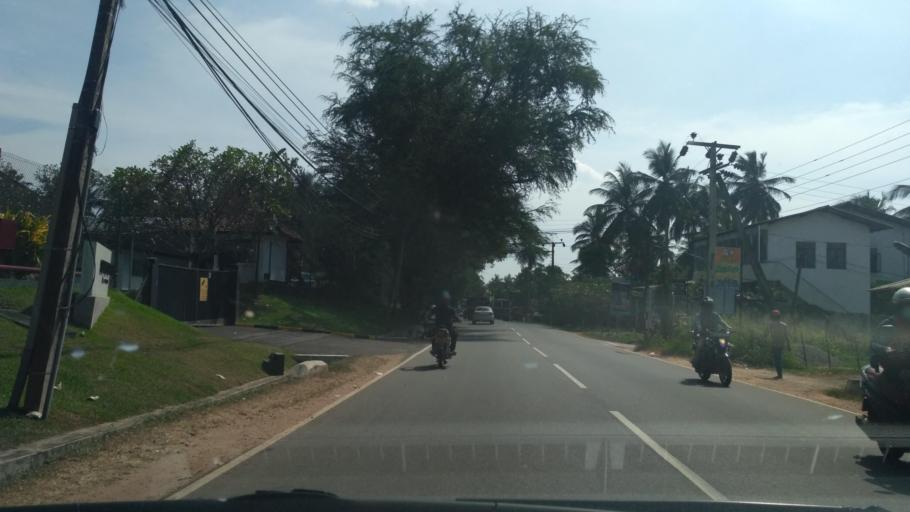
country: LK
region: North Western
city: Kuliyapitiya
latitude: 7.3421
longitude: 80.0308
